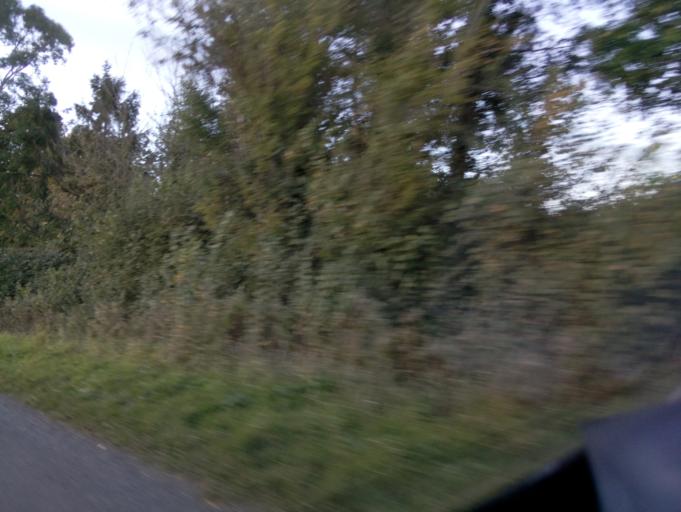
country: GB
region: England
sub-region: Worcestershire
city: Upton upon Severn
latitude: 52.0116
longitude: -2.2850
